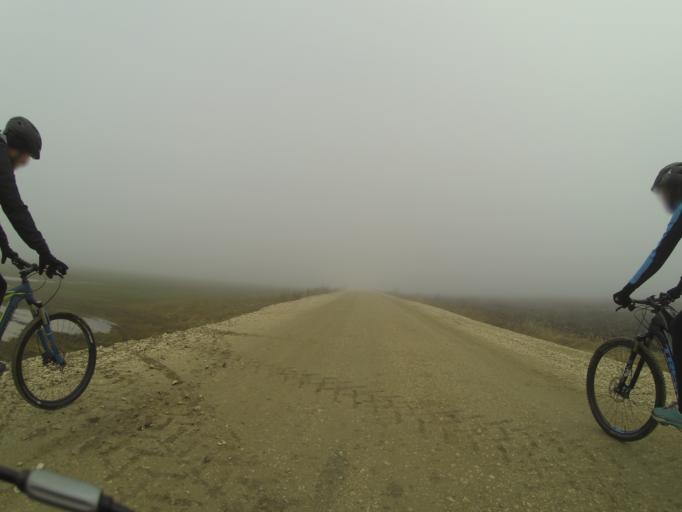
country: RO
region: Mehedinti
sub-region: Comuna Balacita
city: Gvardinita
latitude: 44.4301
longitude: 23.1321
